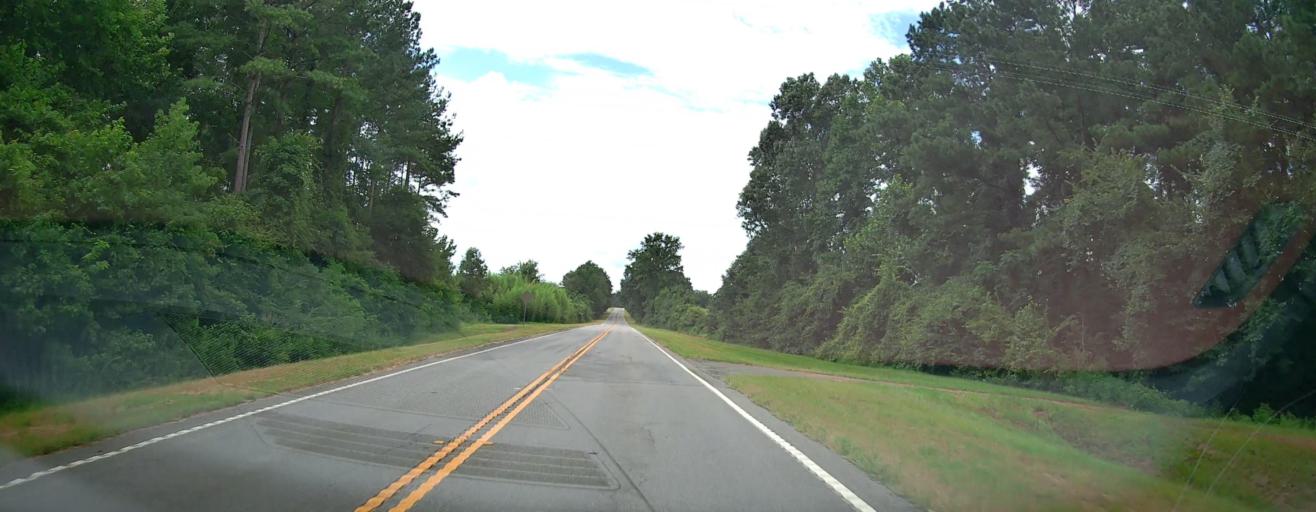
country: US
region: Georgia
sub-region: Macon County
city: Montezuma
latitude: 32.2941
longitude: -83.8952
